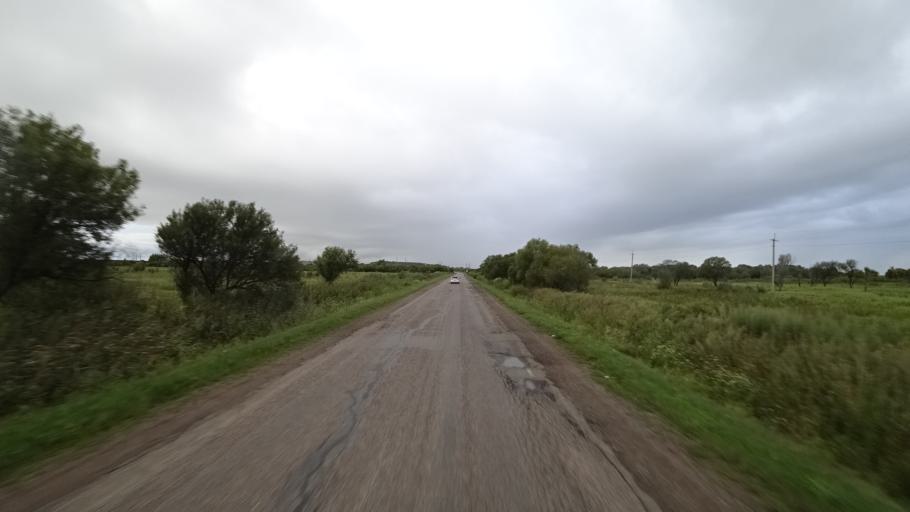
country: RU
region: Primorskiy
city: Chernigovka
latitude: 44.3606
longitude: 132.5559
